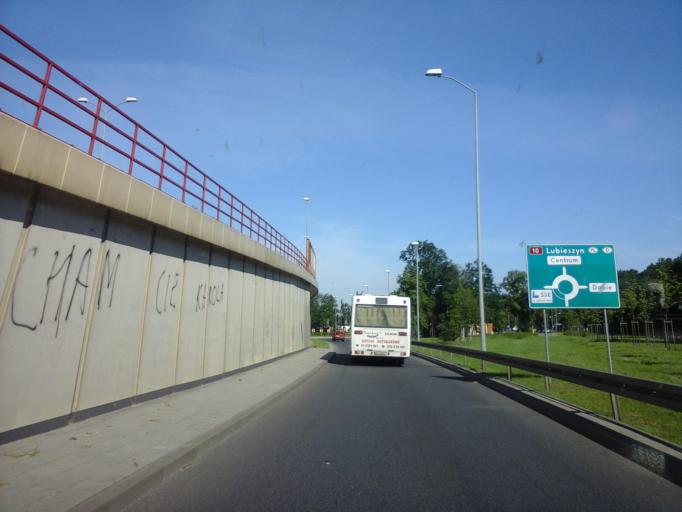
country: PL
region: West Pomeranian Voivodeship
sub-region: Powiat gryfinski
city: Stare Czarnowo
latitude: 53.3809
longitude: 14.6854
